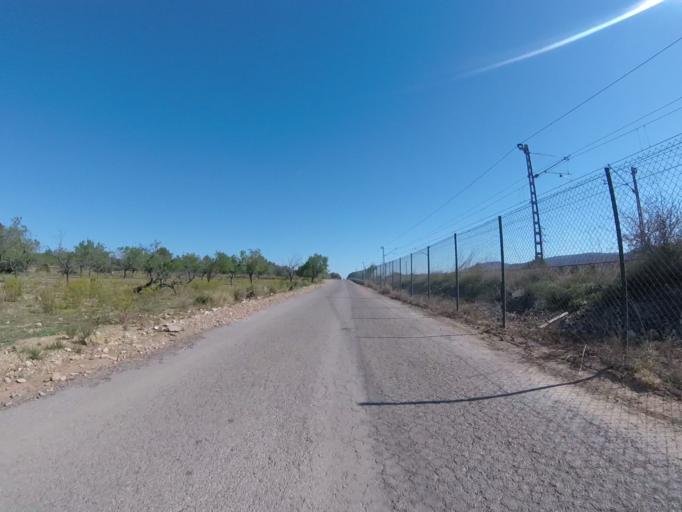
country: ES
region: Valencia
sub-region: Provincia de Castello
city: Alcala de Xivert
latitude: 40.3242
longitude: 0.2395
